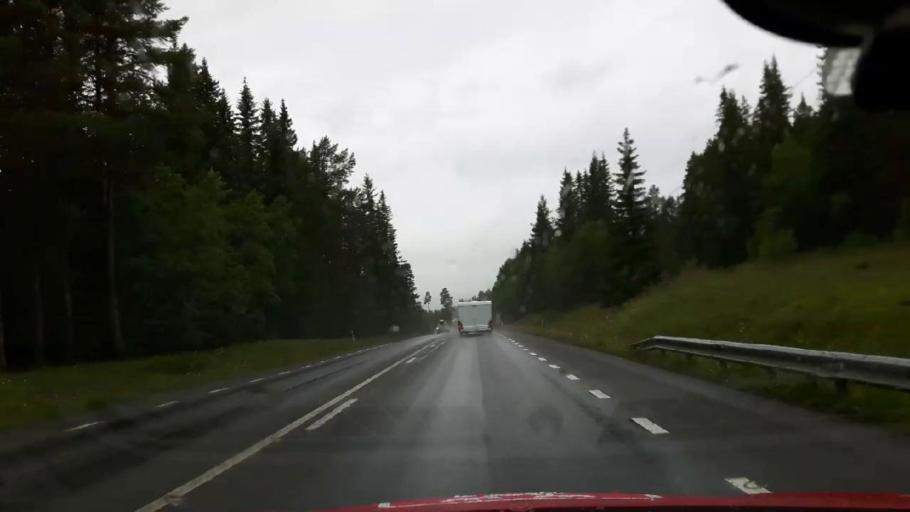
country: SE
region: Jaemtland
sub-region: Are Kommun
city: Jarpen
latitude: 63.3376
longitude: 13.4994
